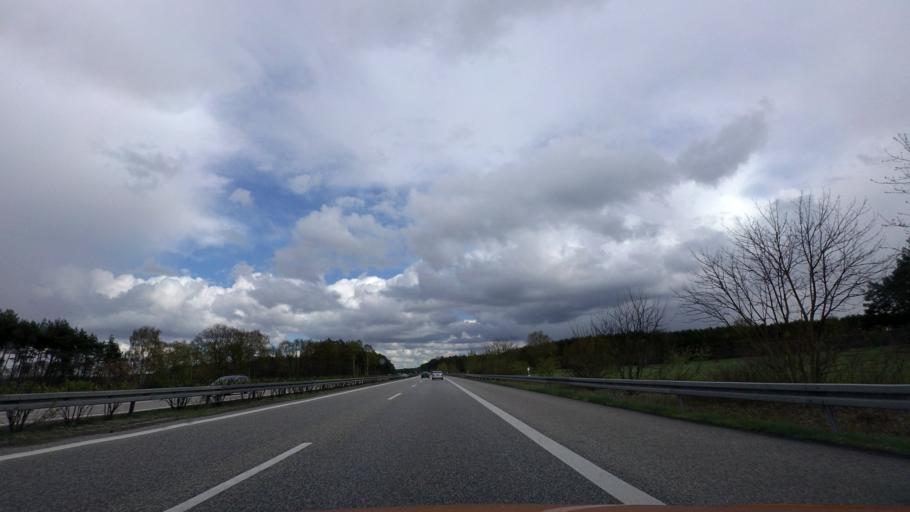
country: DE
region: Mecklenburg-Vorpommern
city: Rastow
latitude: 53.4330
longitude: 11.4044
